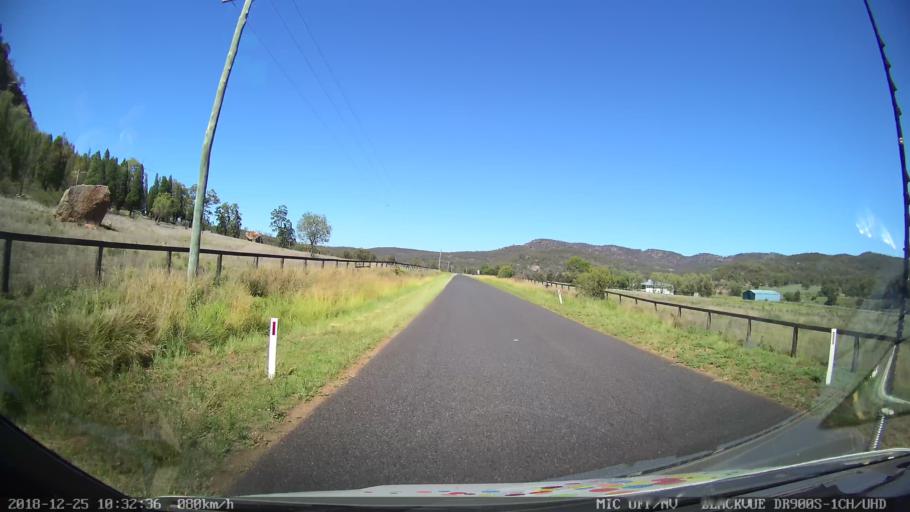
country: AU
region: New South Wales
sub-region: Upper Hunter Shire
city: Merriwa
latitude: -32.3771
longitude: 150.4165
